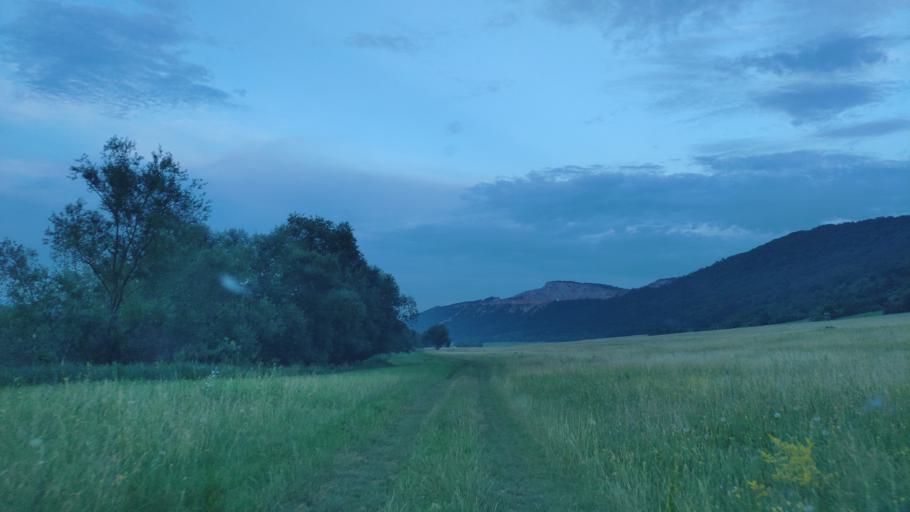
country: SK
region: Kosicky
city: Medzev
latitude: 48.5831
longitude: 20.7781
